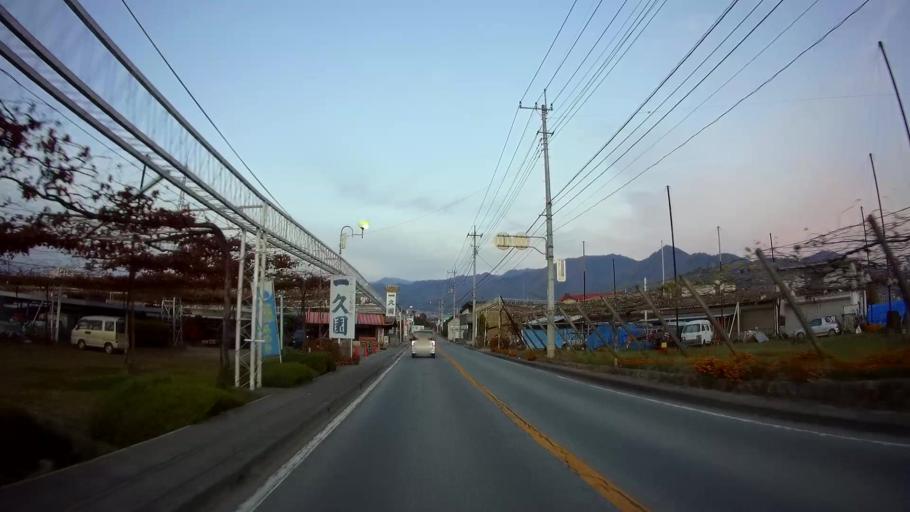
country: JP
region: Yamanashi
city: Enzan
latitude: 35.6646
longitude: 138.7095
